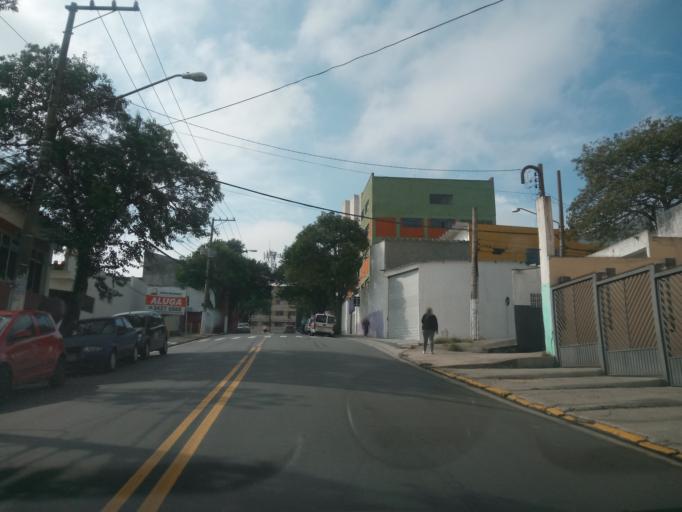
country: BR
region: Sao Paulo
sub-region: Sao Bernardo Do Campo
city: Sao Bernardo do Campo
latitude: -23.6923
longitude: -46.5688
